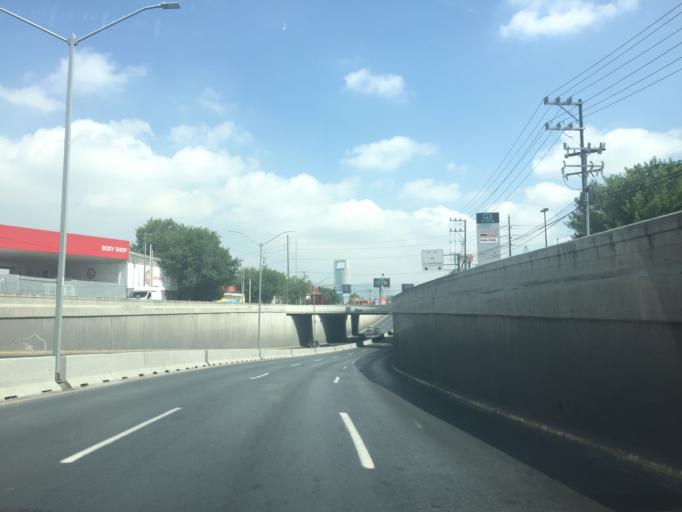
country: MX
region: Nuevo Leon
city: Guadalupe
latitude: 25.6591
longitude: -100.2817
